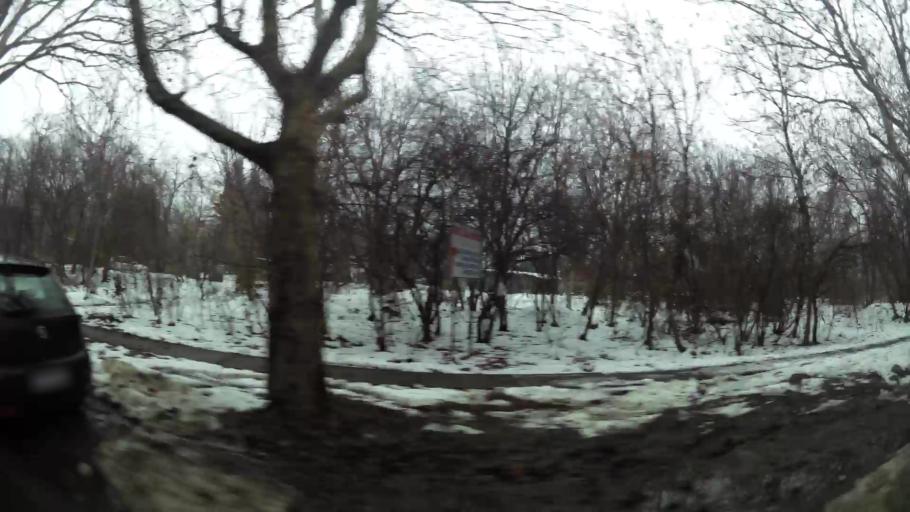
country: RS
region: Central Serbia
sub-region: Belgrade
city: Vozdovac
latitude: 44.7596
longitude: 20.4814
